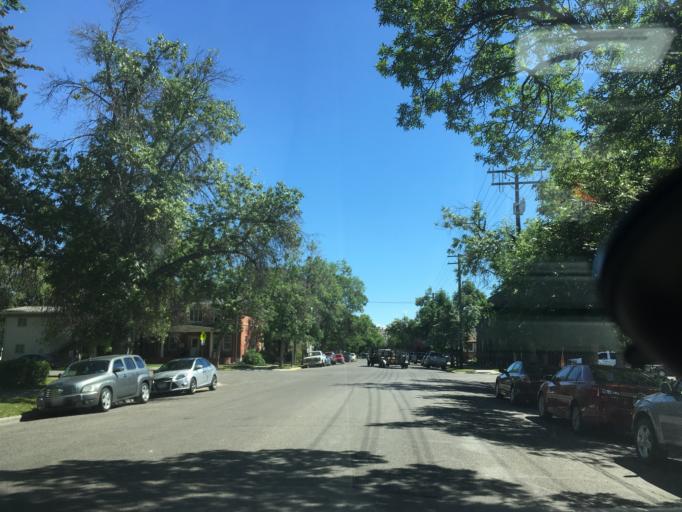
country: US
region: Montana
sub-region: Yellowstone County
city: Billings
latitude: 45.7852
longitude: -108.5150
